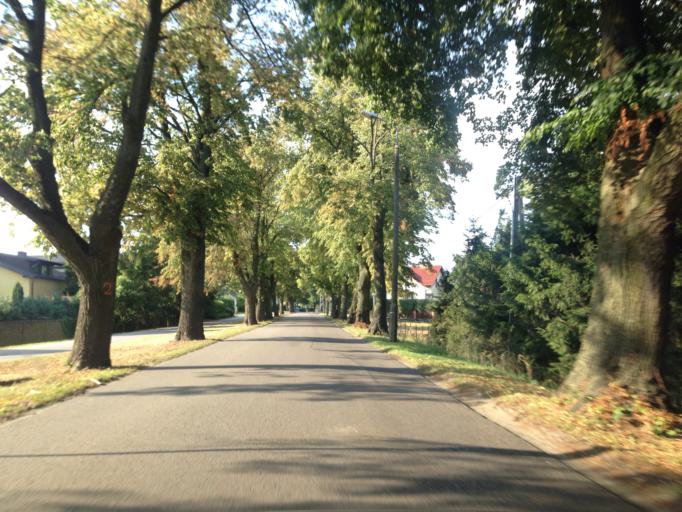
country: PL
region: Warmian-Masurian Voivodeship
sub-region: Powiat ilawski
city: Ilawa
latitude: 53.6137
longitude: 19.5690
